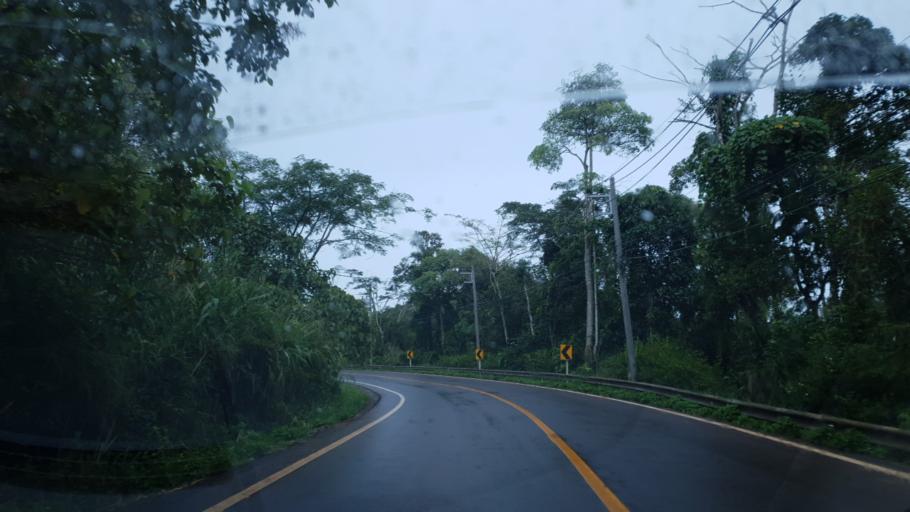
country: TH
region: Mae Hong Son
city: Ban Huai I Huak
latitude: 18.1367
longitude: 98.0769
